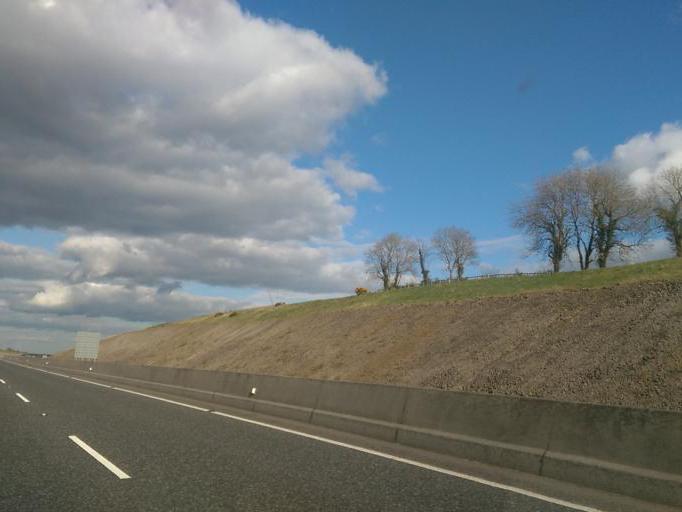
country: IE
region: Leinster
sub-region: An Iarmhi
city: Rochfortbridge
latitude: 53.3939
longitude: -7.3430
